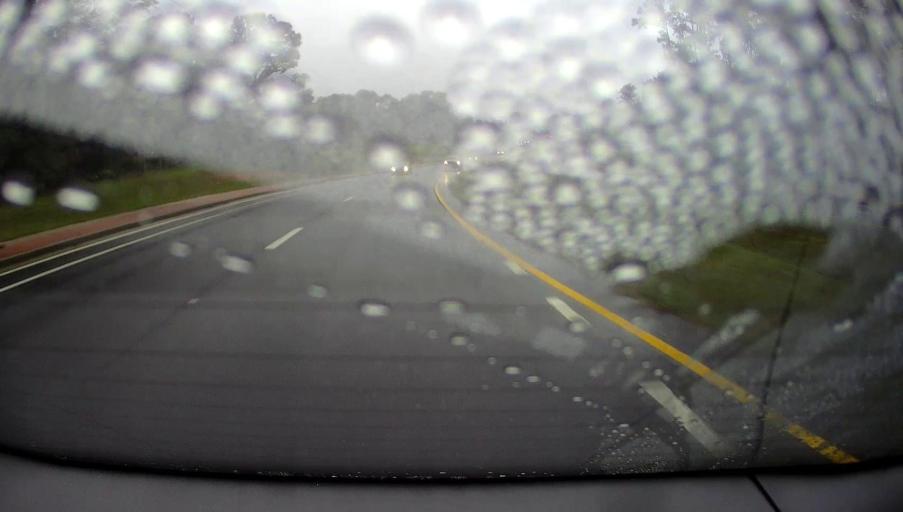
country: US
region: Georgia
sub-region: Houston County
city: Robins Air Force Base
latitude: 32.5529
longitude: -83.6204
